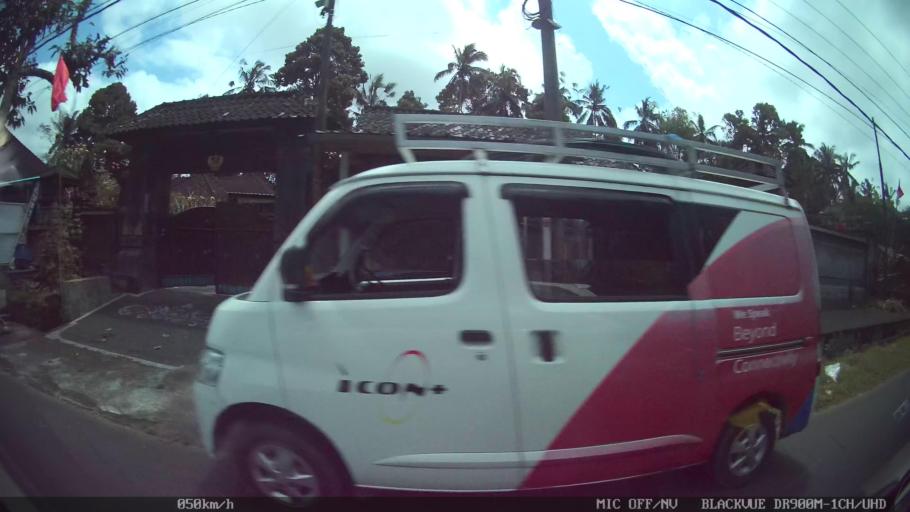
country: ID
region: Bali
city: Banjar Bebalang
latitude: -8.4736
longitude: 115.3781
